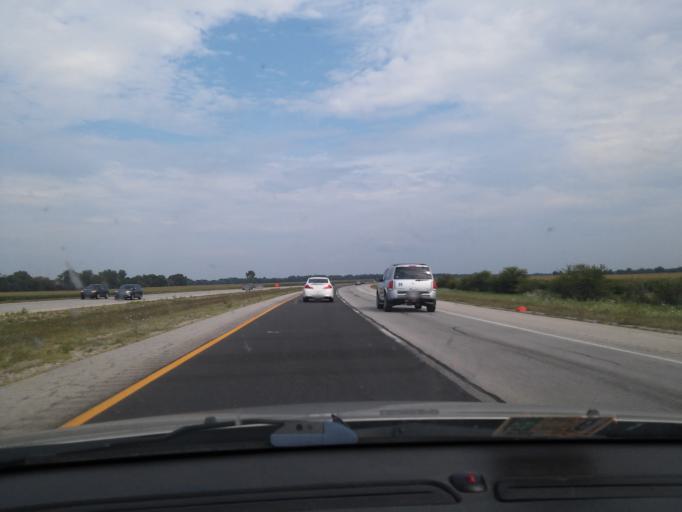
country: US
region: Ohio
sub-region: Fayette County
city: Jeffersonville
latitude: 39.5864
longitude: -83.5448
